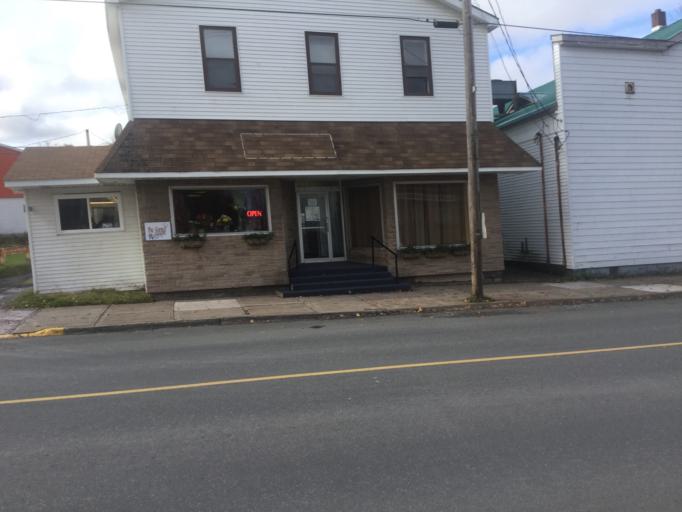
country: CA
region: Nova Scotia
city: New Glasgow
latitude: 45.5606
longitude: -62.6596
